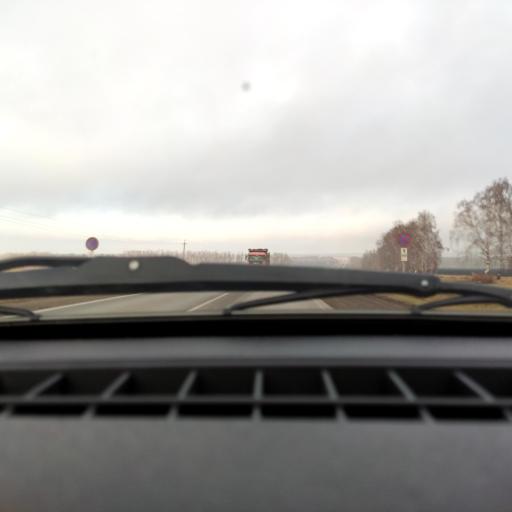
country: RU
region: Bashkortostan
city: Chishmy
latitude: 54.6372
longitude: 55.3759
